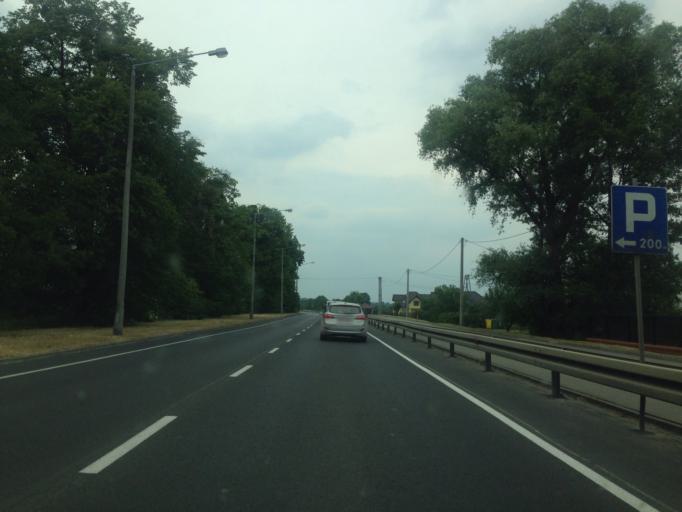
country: PL
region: Kujawsko-Pomorskie
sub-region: Grudziadz
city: Grudziadz
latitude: 53.5038
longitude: 18.8405
